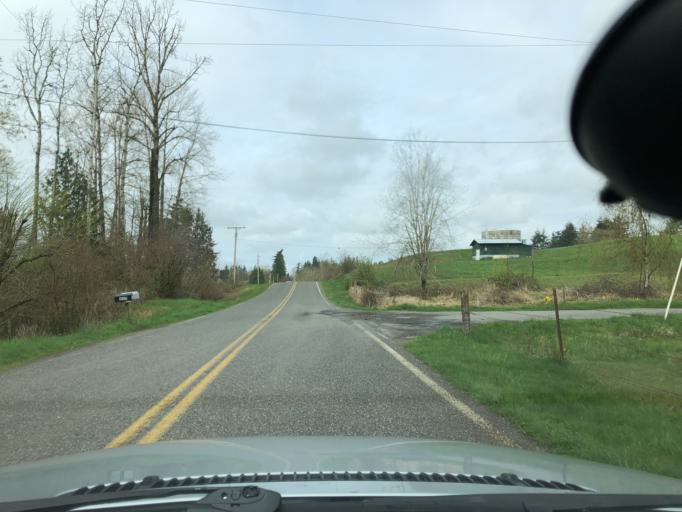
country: US
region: Washington
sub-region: Whatcom County
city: Lynden
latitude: 48.9831
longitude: -122.5346
